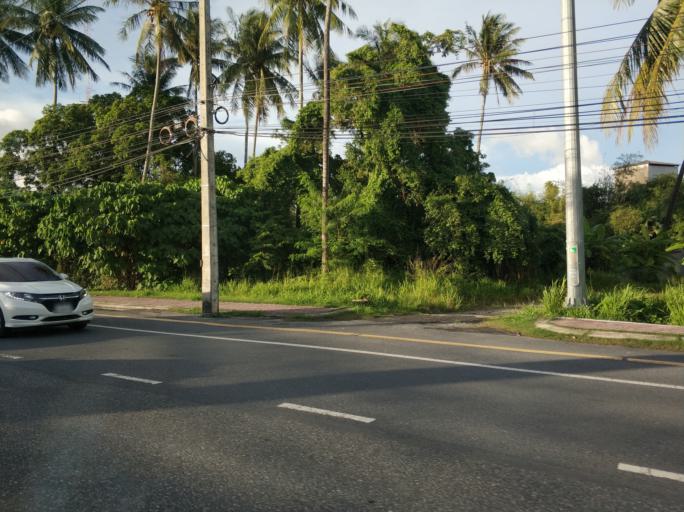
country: TH
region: Phuket
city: Kathu
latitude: 7.9022
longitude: 98.3370
